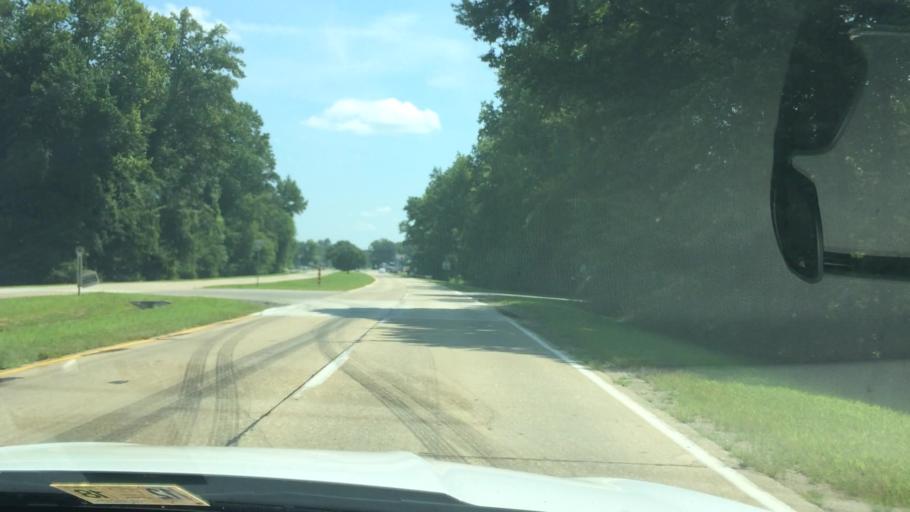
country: US
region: Virginia
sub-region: New Kent County
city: New Kent
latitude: 37.4427
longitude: -77.0483
